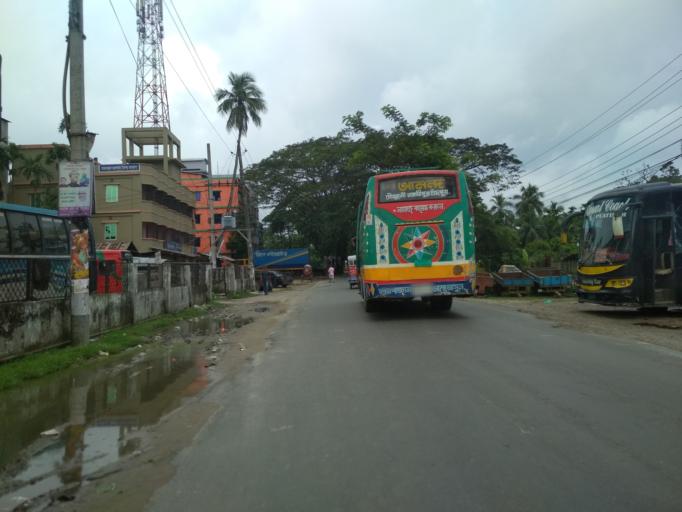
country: BD
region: Chittagong
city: Lakshmipur
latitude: 22.9464
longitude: 90.8124
